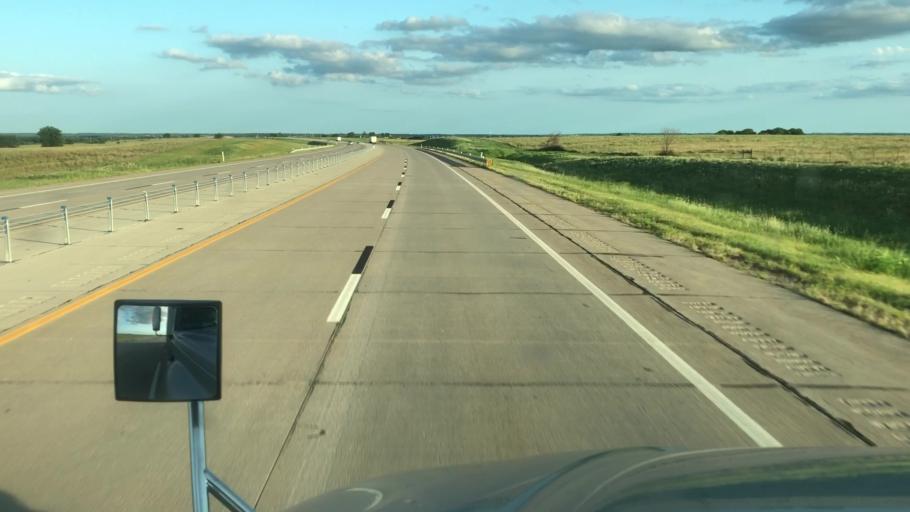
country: US
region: Oklahoma
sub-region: Pawnee County
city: Pawnee
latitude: 36.3463
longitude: -97.0275
